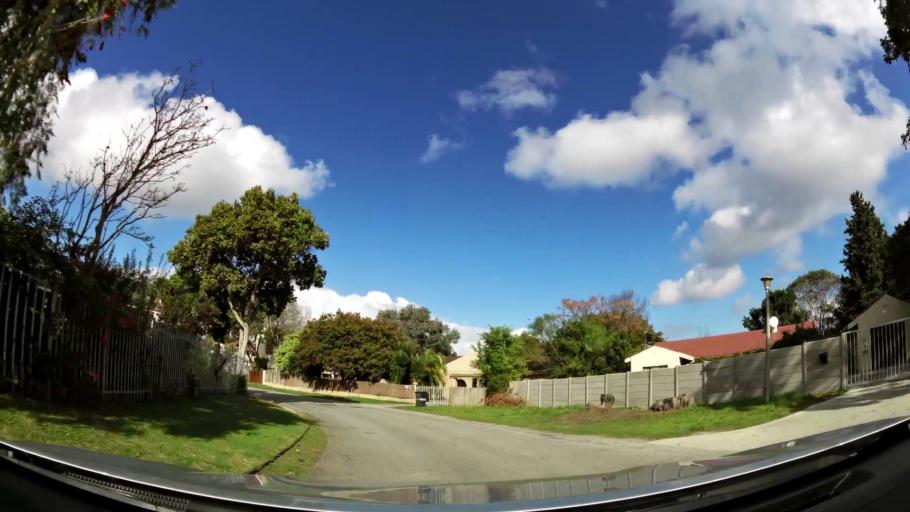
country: ZA
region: Western Cape
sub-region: Eden District Municipality
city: Knysna
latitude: -34.0415
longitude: 23.0687
